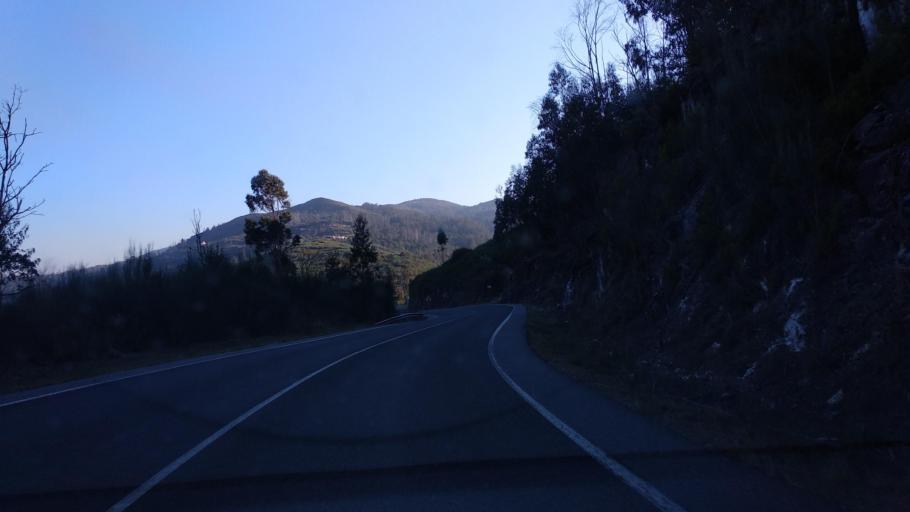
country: ES
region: Galicia
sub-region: Provincia de Pontevedra
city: Ponte Caldelas
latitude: 42.3449
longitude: -8.5423
